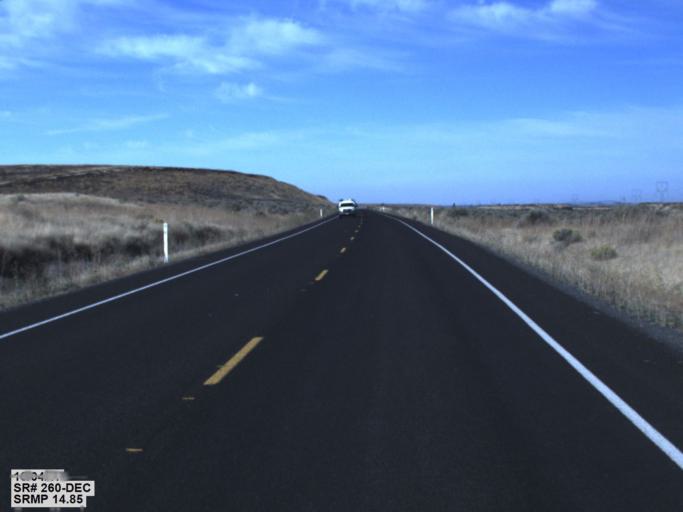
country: US
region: Washington
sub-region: Franklin County
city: Connell
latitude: 46.6307
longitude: -118.7399
